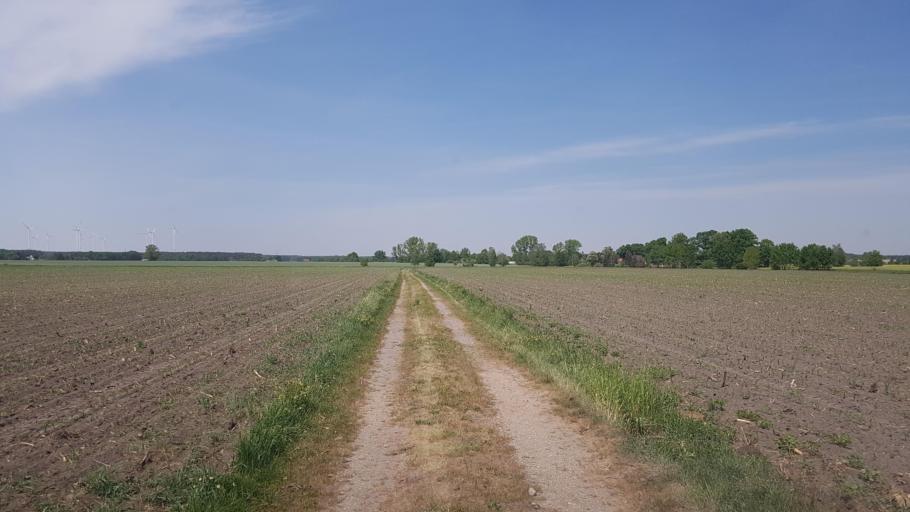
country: DE
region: Brandenburg
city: Sallgast
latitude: 51.5963
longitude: 13.8540
